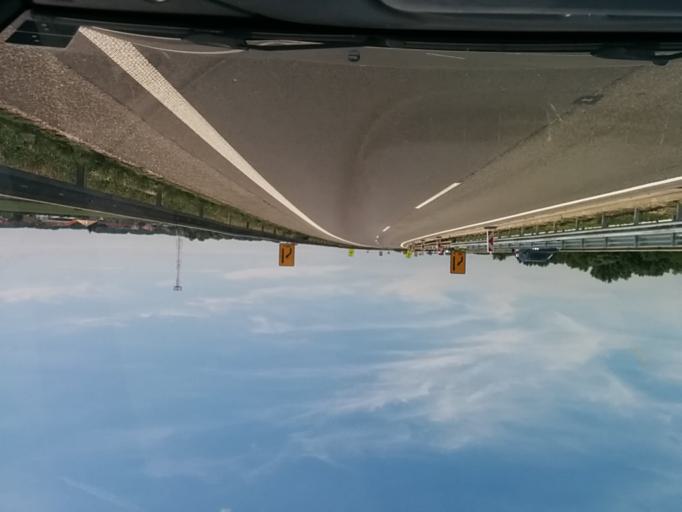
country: SK
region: Trnavsky
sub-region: Okres Galanta
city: Galanta
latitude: 48.2561
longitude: 17.7731
